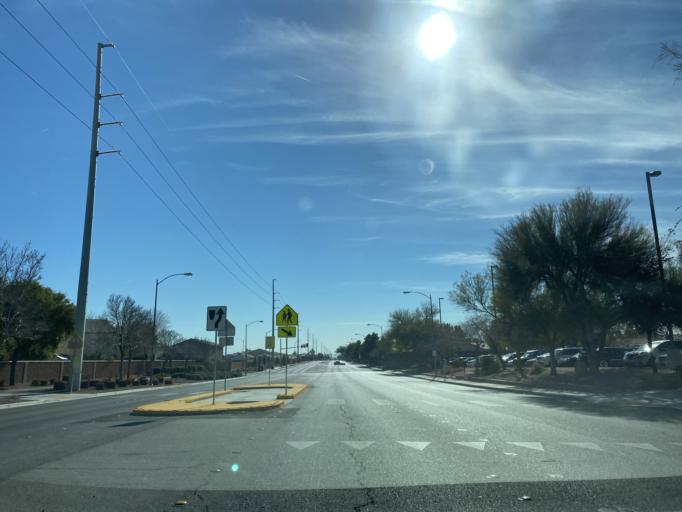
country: US
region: Nevada
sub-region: Clark County
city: North Las Vegas
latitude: 36.2663
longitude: -115.1440
